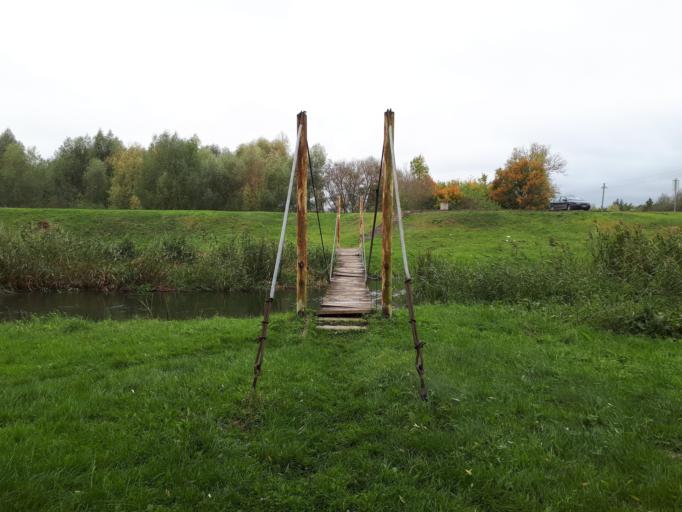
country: LT
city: Kalvarija
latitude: 54.4064
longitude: 23.2125
